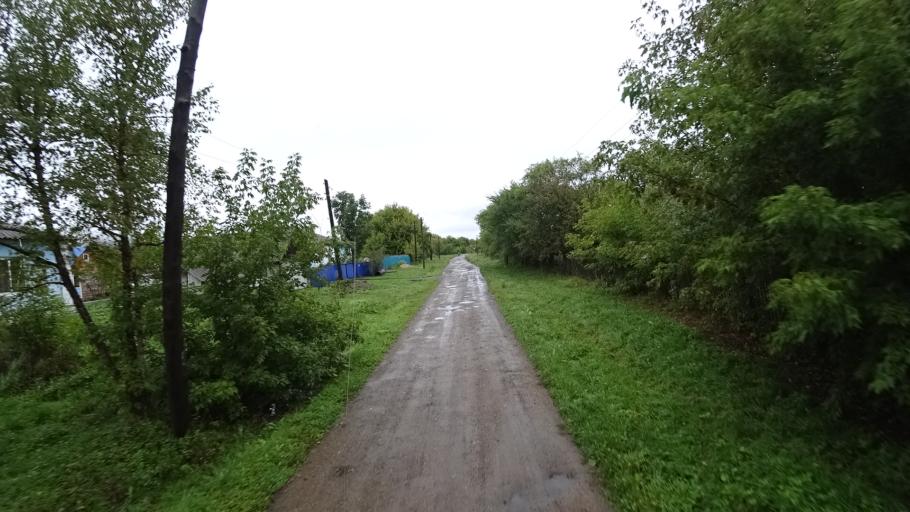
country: RU
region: Primorskiy
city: Monastyrishche
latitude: 44.2548
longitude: 132.4244
